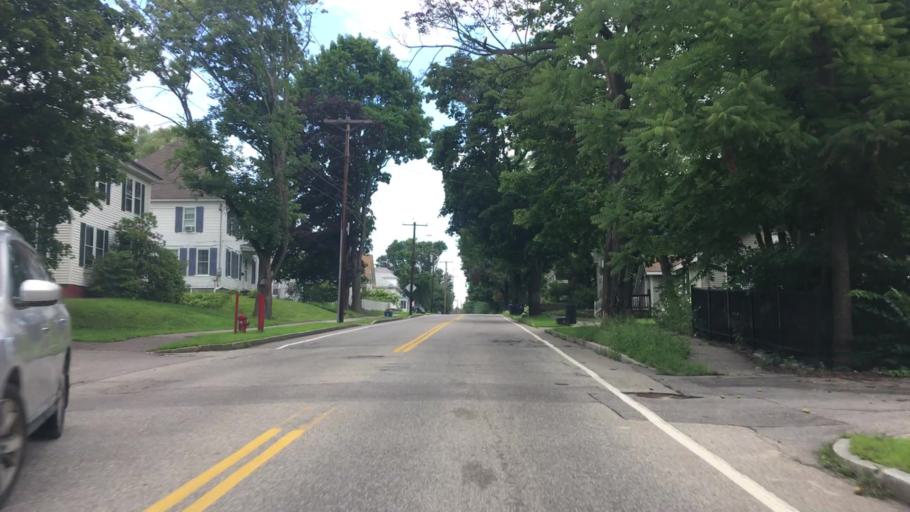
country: US
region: New Hampshire
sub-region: Belknap County
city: Laconia
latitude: 43.5501
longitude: -71.4667
